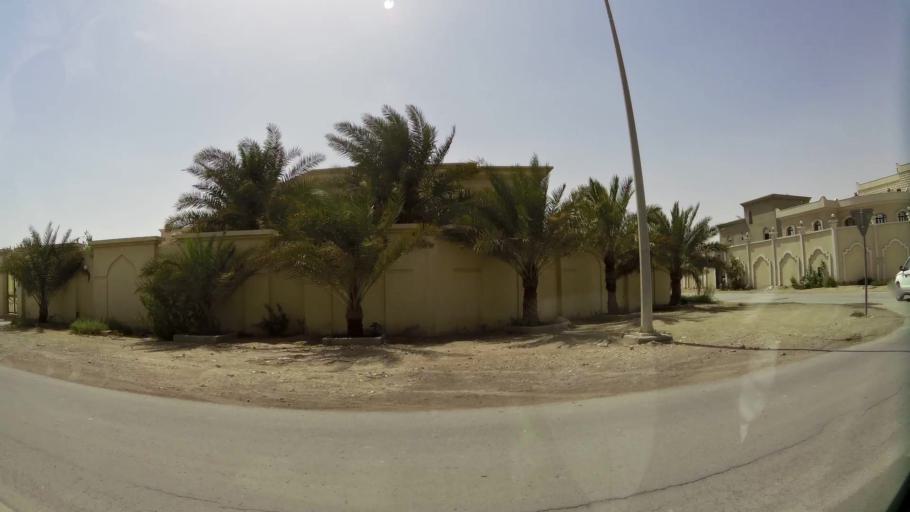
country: QA
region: Baladiyat Umm Salal
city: Umm Salal Muhammad
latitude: 25.3783
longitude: 51.4249
